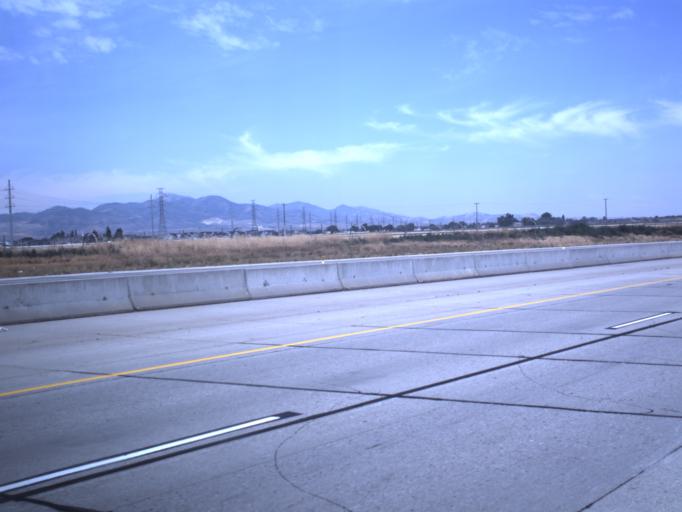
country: US
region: Utah
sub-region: Salt Lake County
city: Riverton
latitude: 40.5109
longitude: -111.9839
